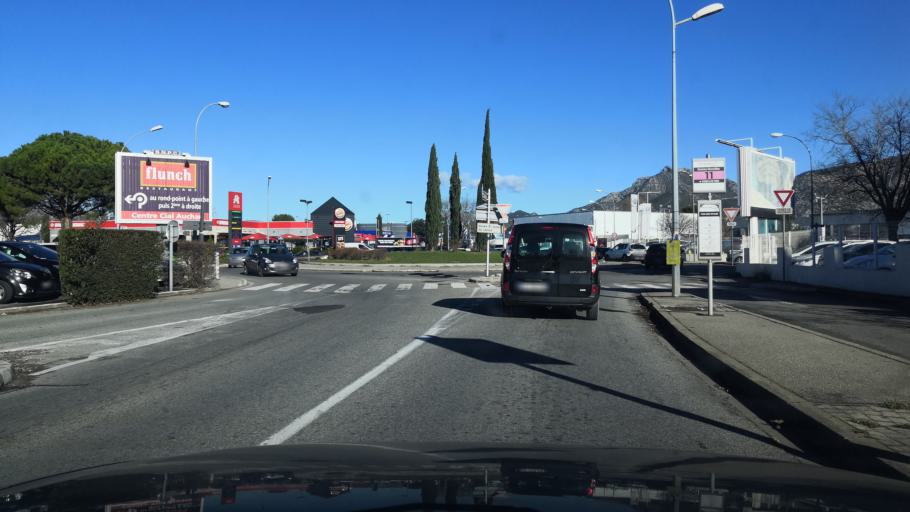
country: FR
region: Provence-Alpes-Cote d'Azur
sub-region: Departement des Bouches-du-Rhone
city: Aubagne
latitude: 43.2908
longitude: 5.5932
